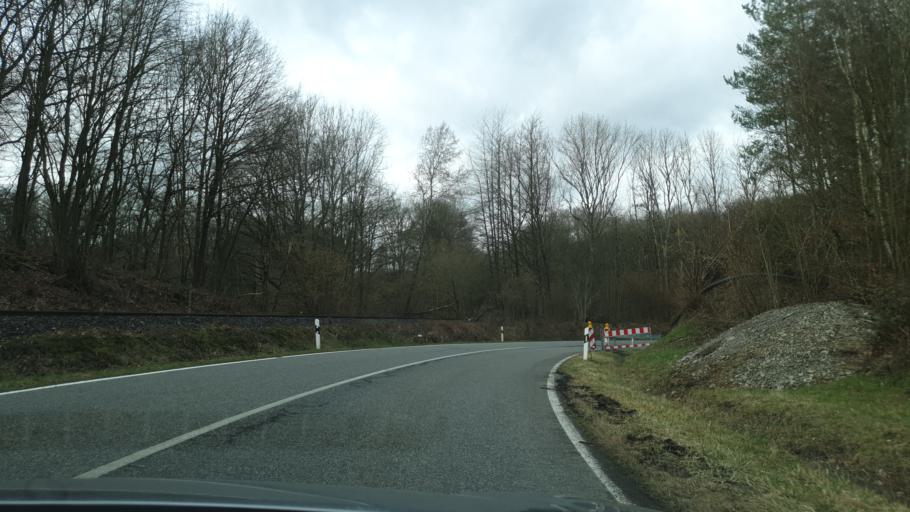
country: DE
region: Rheinland-Pfalz
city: Puderbach
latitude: 50.6029
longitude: 7.6066
